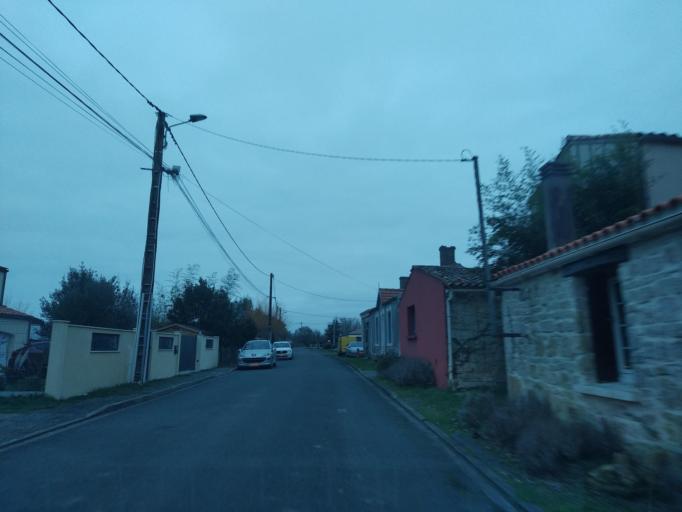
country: FR
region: Pays de la Loire
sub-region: Departement de la Vendee
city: Triaize
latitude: 46.4108
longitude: -1.2615
